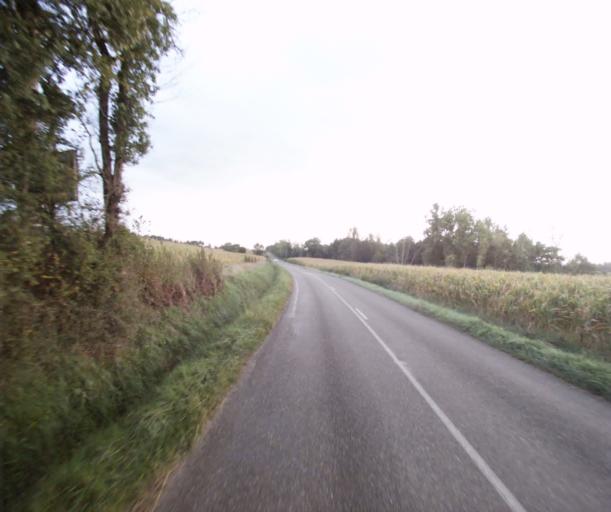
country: FR
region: Midi-Pyrenees
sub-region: Departement du Gers
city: Cazaubon
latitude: 43.9166
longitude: -0.0796
